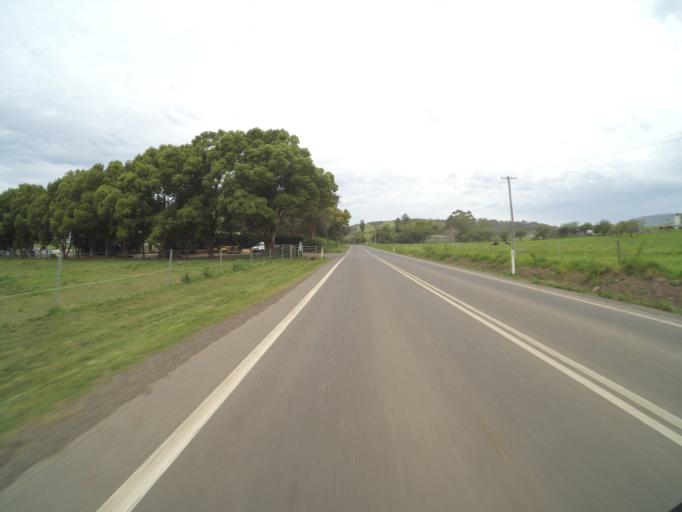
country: AU
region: New South Wales
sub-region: Kiama
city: Jamberoo
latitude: -34.6504
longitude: 150.7923
